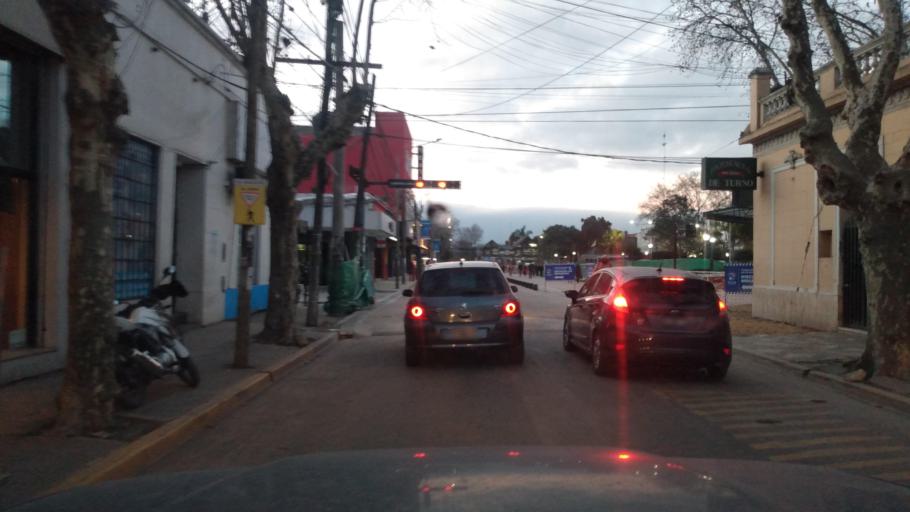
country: AR
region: Buenos Aires
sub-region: Partido de Pilar
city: Pilar
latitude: -34.4595
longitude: -58.9146
